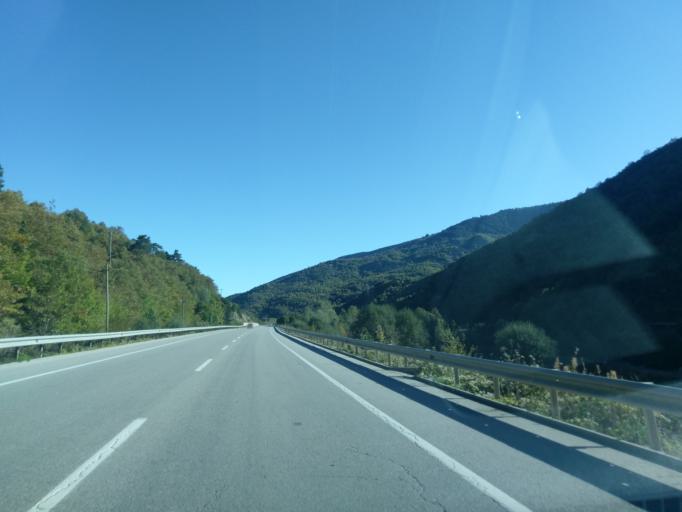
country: TR
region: Sinop
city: Erfelek
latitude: 41.7245
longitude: 34.9413
